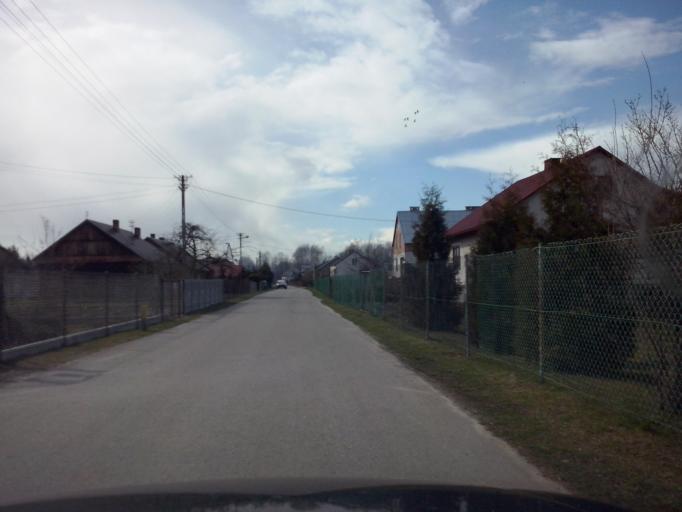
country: PL
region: Subcarpathian Voivodeship
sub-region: Powiat nizanski
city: Bieliny
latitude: 50.4418
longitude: 22.3041
